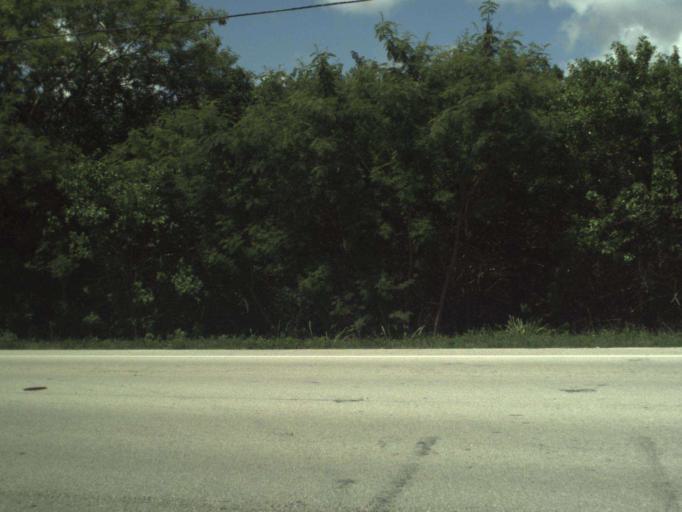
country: US
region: Florida
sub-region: Indian River County
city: Vero Beach
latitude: 27.6517
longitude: -80.3837
